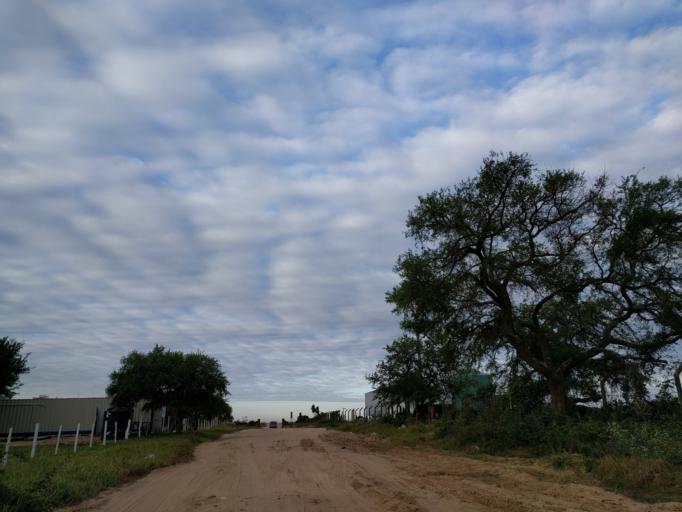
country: BO
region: Santa Cruz
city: Santa Rita
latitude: -17.8935
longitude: -63.2637
